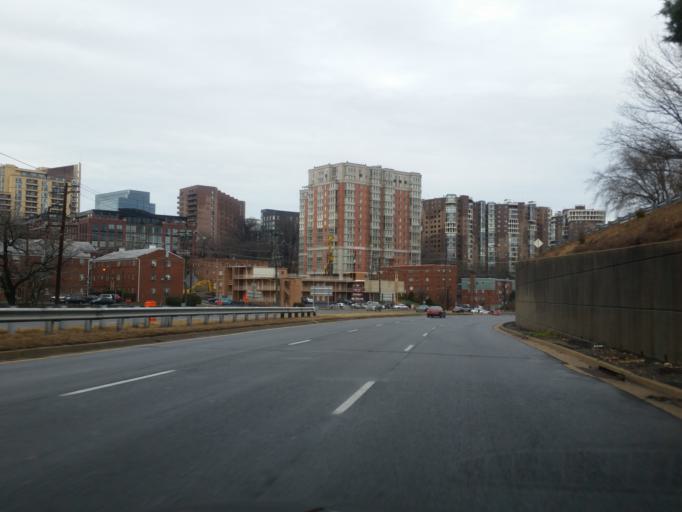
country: US
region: Virginia
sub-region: Arlington County
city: Arlington
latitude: 38.8896
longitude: -77.0778
